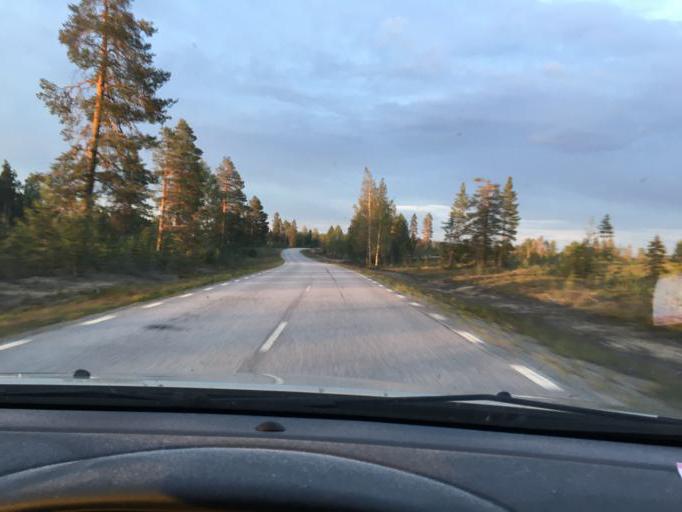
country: SE
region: Norrbotten
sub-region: Kalix Kommun
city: Toere
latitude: 66.0530
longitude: 22.4761
